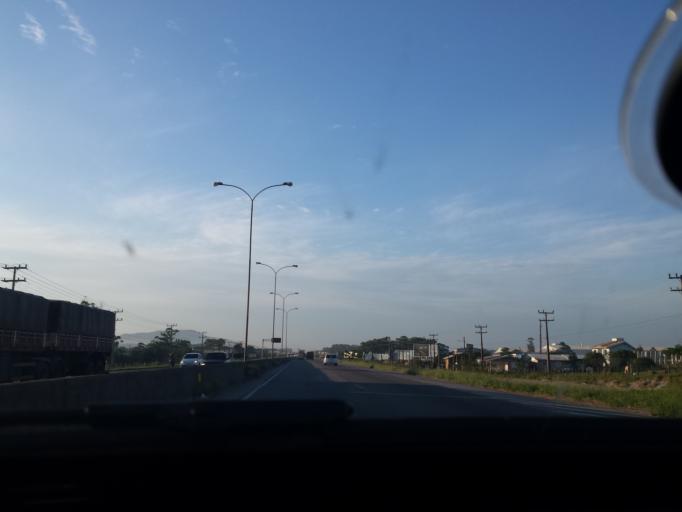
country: BR
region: Santa Catarina
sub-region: Imbituba
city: Imbituba
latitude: -28.1655
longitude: -48.6939
